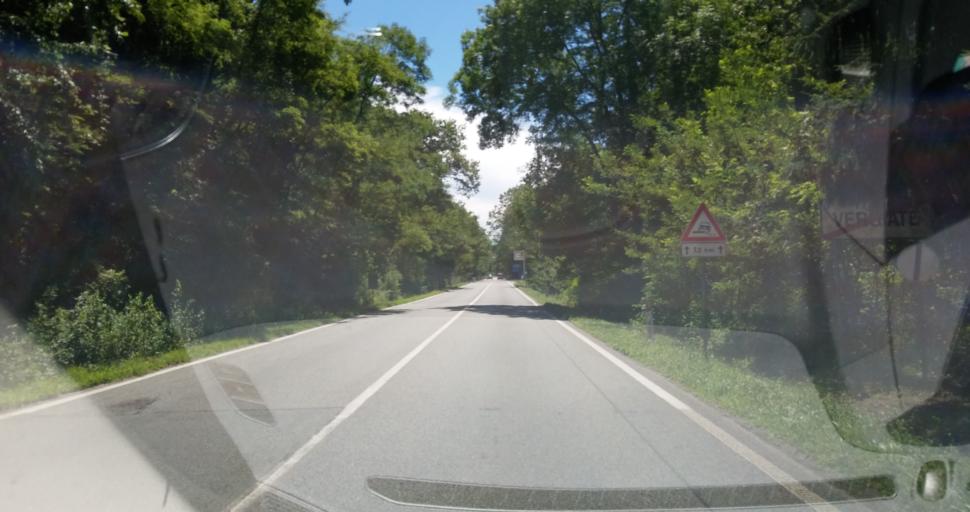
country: IT
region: Lombardy
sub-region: Provincia di Varese
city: Vergiate
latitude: 45.7082
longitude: 8.6969
